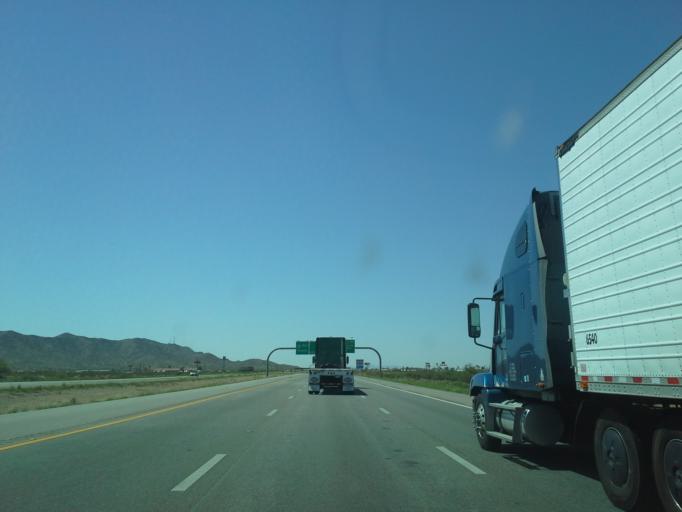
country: US
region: Arizona
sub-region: Pinal County
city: Arizona City
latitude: 32.8015
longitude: -111.6582
